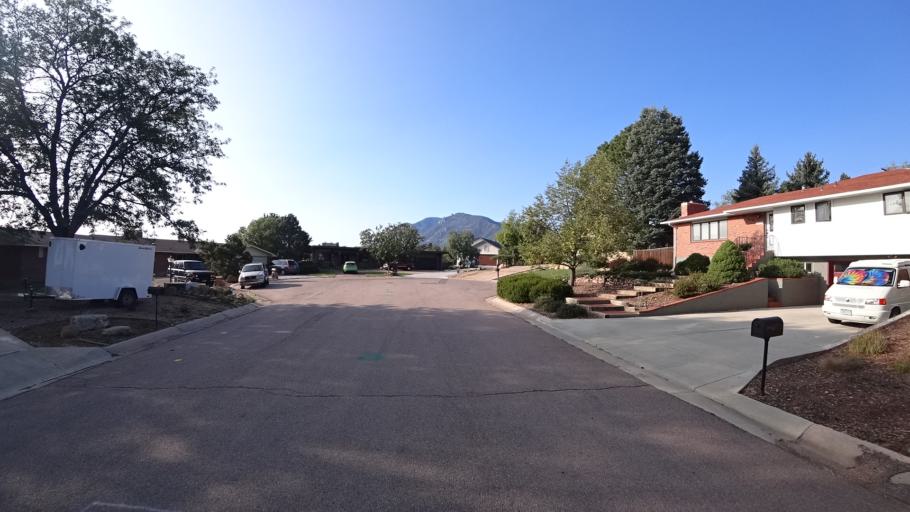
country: US
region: Colorado
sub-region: El Paso County
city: Colorado Springs
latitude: 38.8152
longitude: -104.8542
